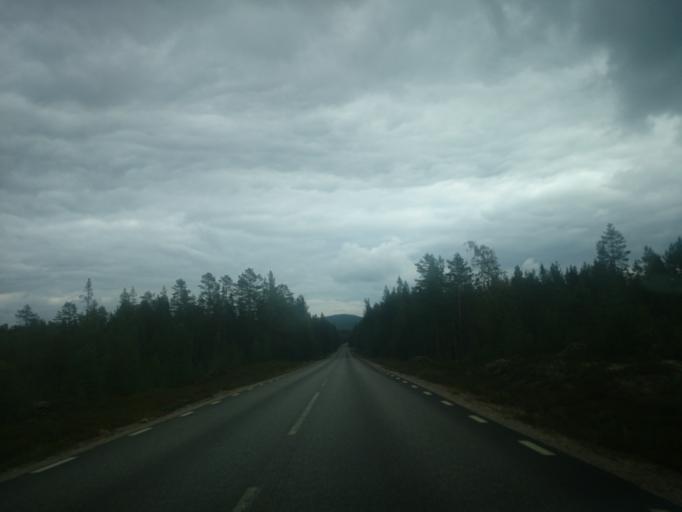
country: SE
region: Jaemtland
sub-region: Harjedalens Kommun
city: Sveg
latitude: 61.9961
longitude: 14.9875
